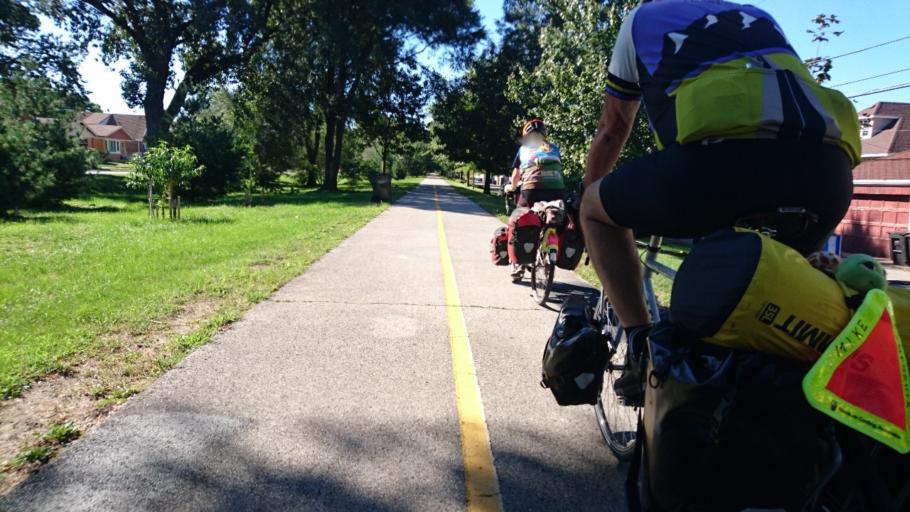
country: US
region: Indiana
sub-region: Lake County
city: Whiting
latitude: 41.7023
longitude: -87.5285
